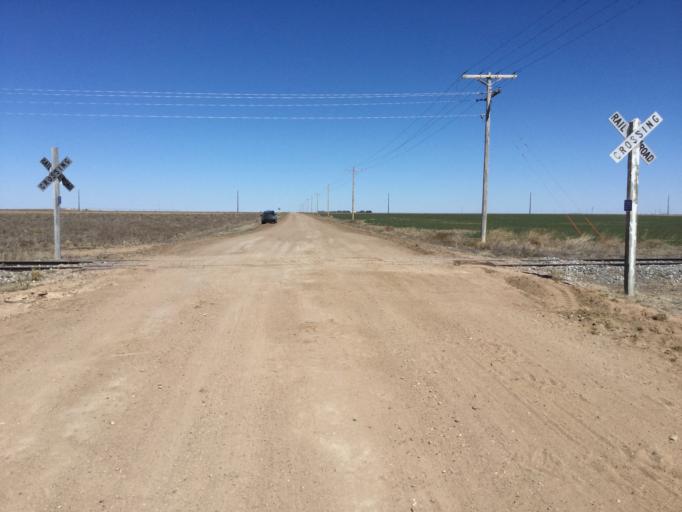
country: US
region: Kansas
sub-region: Grant County
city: Ulysses
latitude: 37.5690
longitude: -101.4172
